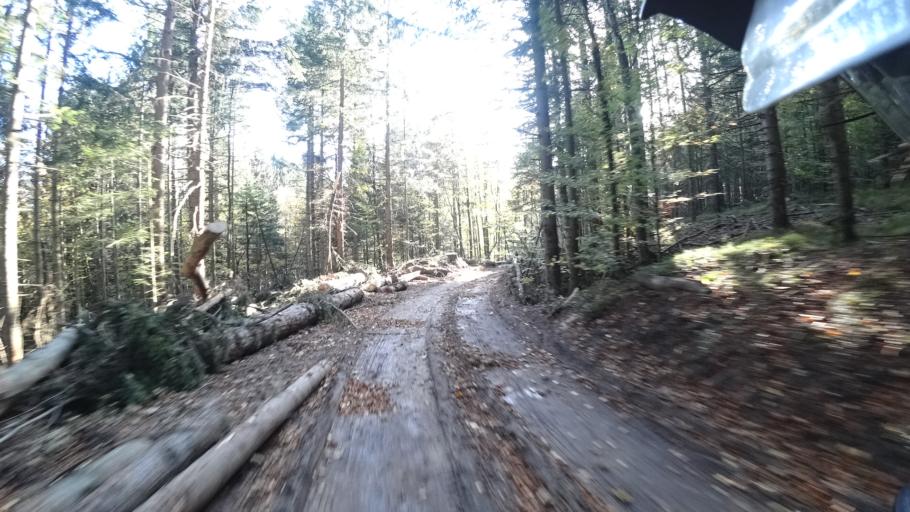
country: HR
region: Karlovacka
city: Plaski
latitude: 44.9510
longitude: 15.4499
